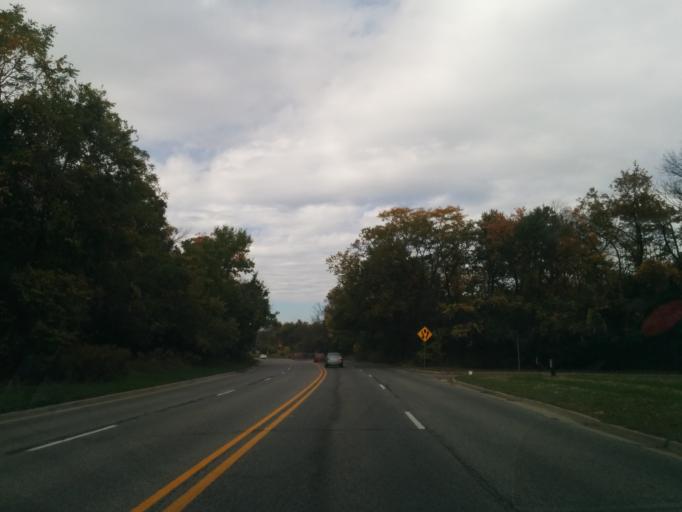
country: US
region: Illinois
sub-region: Cook County
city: River Grove
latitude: 41.9205
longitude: -87.8389
